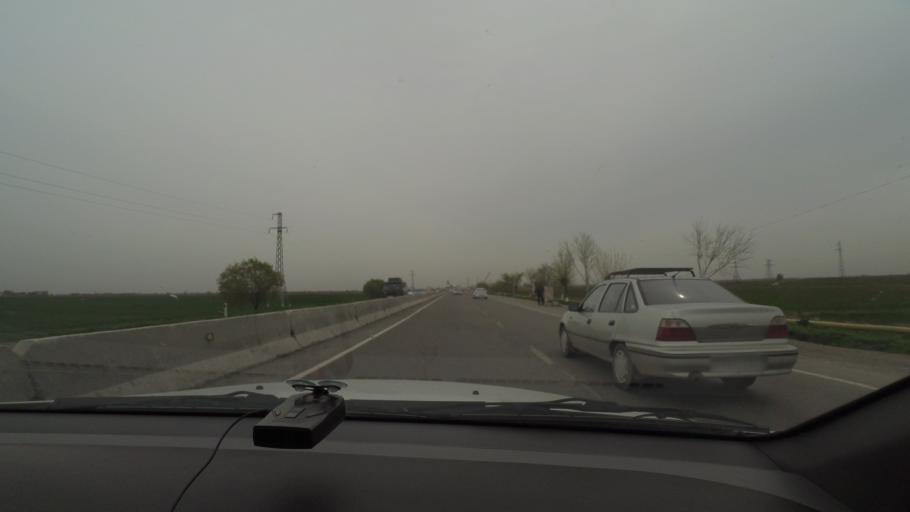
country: KZ
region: Ongtustik Qazaqstan
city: Myrzakent
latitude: 40.5613
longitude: 68.3806
